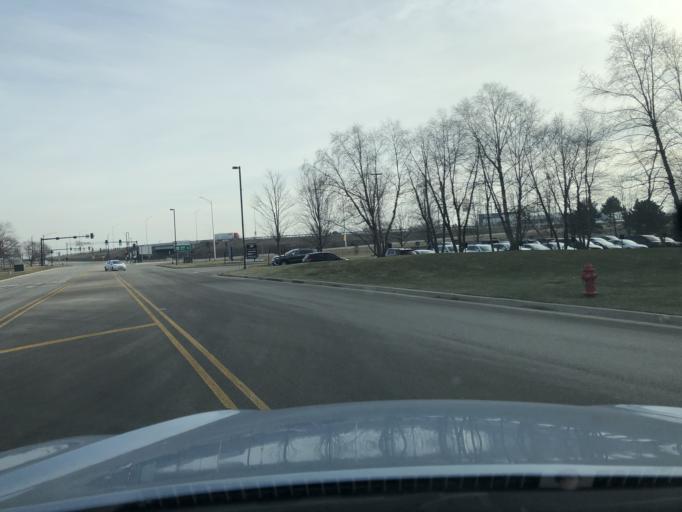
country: US
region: Illinois
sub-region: DuPage County
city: Itasca
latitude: 41.9858
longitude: -88.0070
